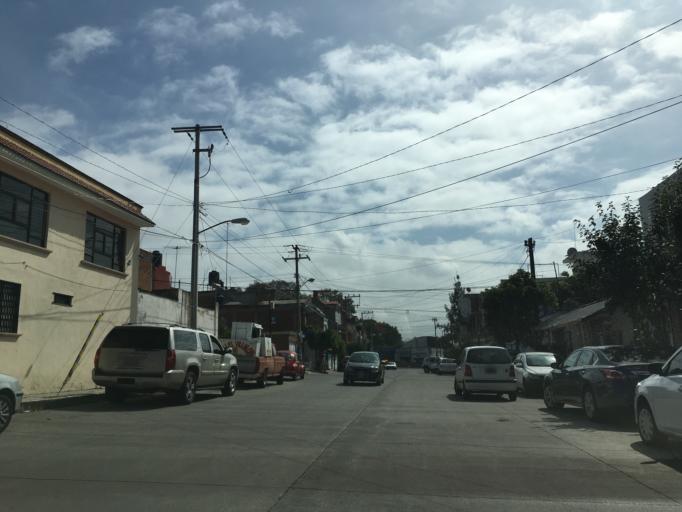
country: MX
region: Michoacan
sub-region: Morelia
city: Morelos
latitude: 19.6724
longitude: -101.2231
